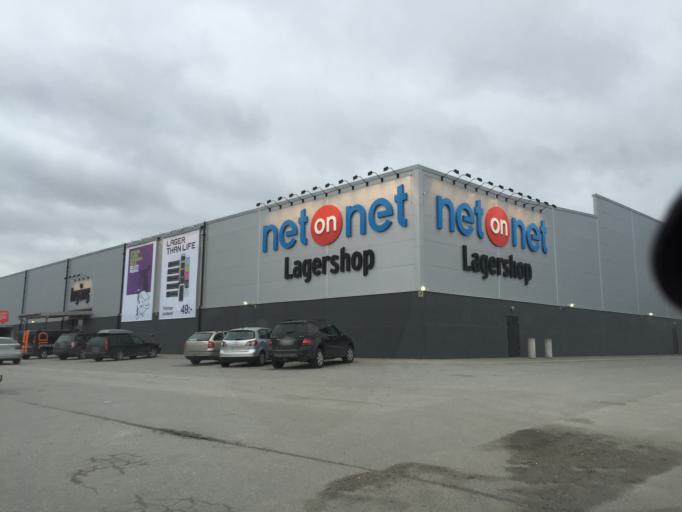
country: SE
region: OErebro
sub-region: Orebro Kommun
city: Orebro
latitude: 59.2667
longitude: 15.1697
